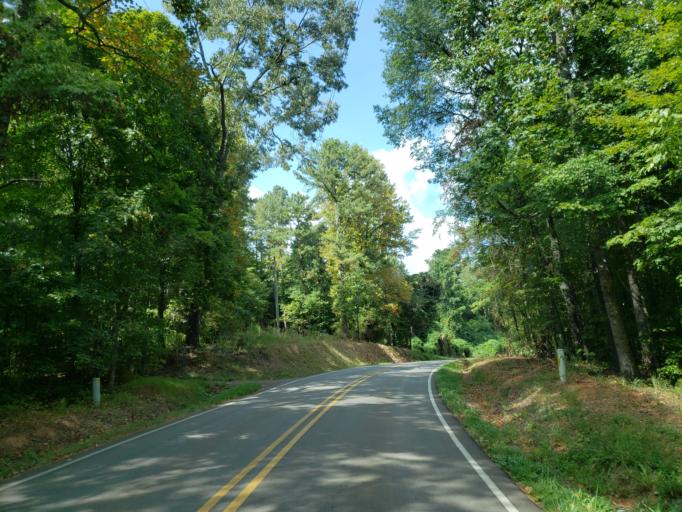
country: US
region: Georgia
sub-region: Pickens County
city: Jasper
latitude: 34.4272
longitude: -84.4404
